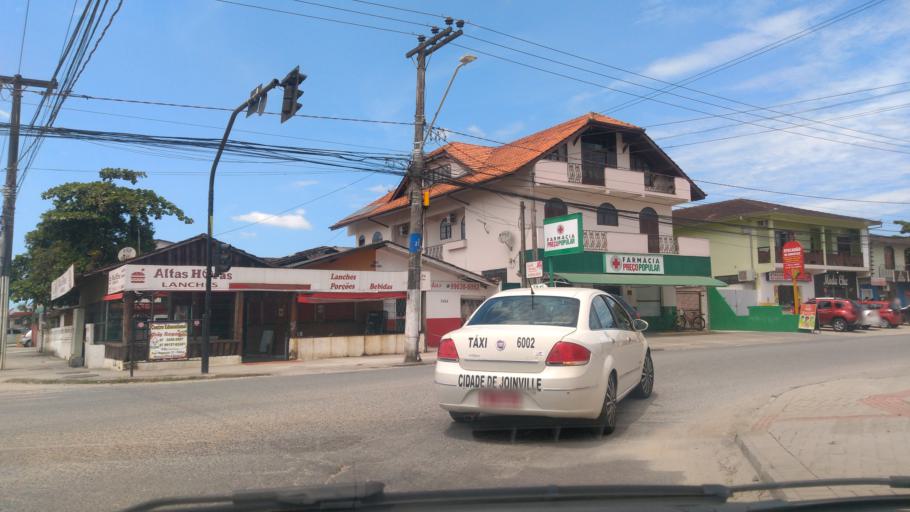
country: BR
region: Santa Catarina
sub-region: Joinville
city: Joinville
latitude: -26.3202
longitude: -48.8161
